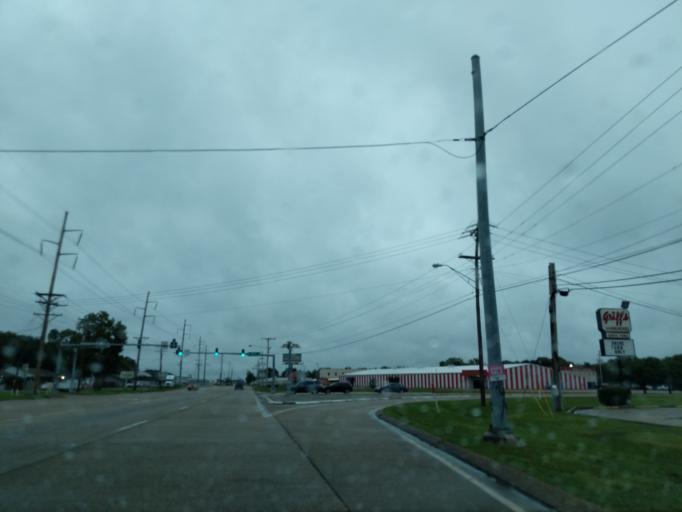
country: US
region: Louisiana
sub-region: Bossier Parish
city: Bossier City
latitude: 32.5216
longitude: -93.6952
